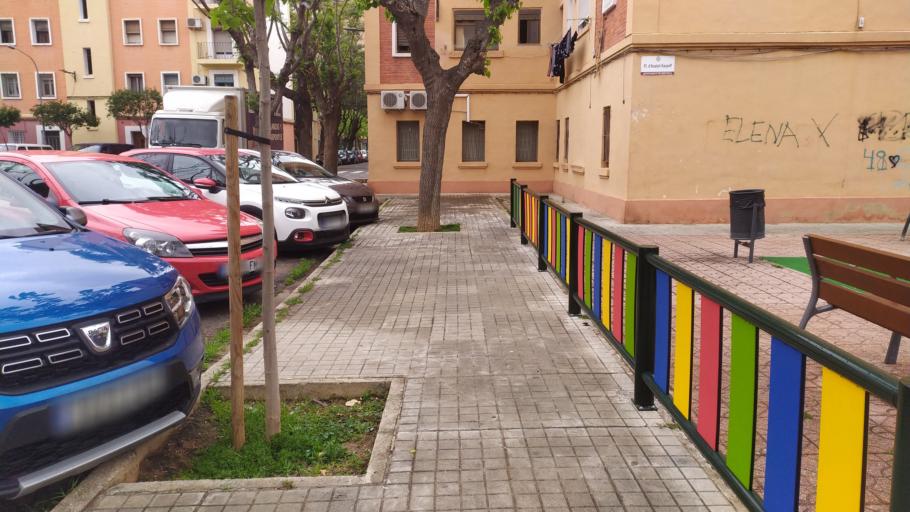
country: ES
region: Valencia
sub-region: Provincia de Valencia
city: Mislata
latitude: 39.4660
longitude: -0.4158
